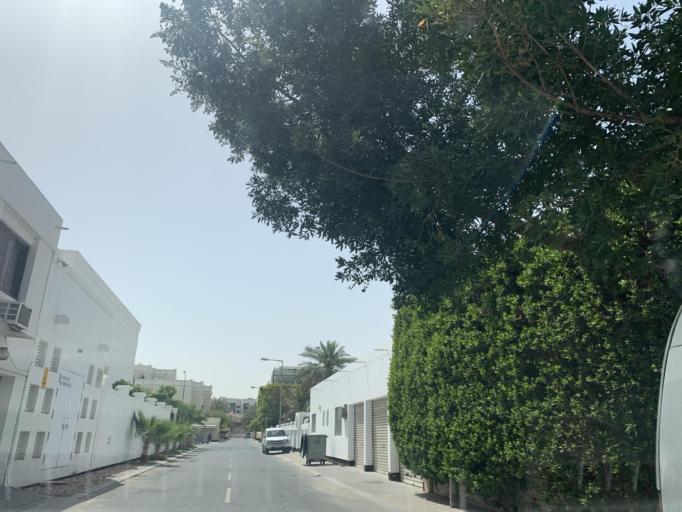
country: BH
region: Manama
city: Jidd Hafs
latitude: 26.2196
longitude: 50.5595
